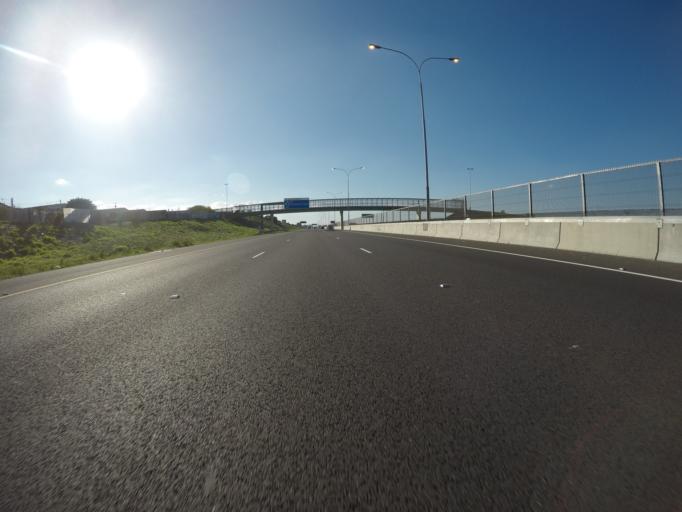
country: ZA
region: Western Cape
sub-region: City of Cape Town
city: Kraaifontein
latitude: -33.9688
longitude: 18.6544
